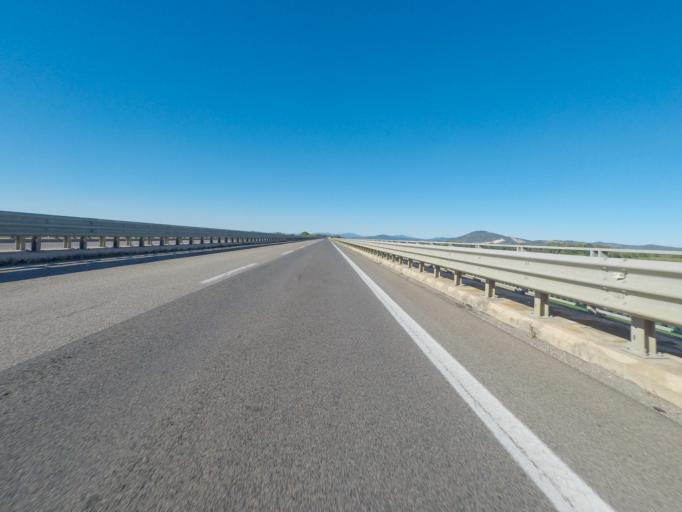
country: IT
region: Tuscany
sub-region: Provincia di Grosseto
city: Grosseto
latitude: 42.7523
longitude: 11.1435
